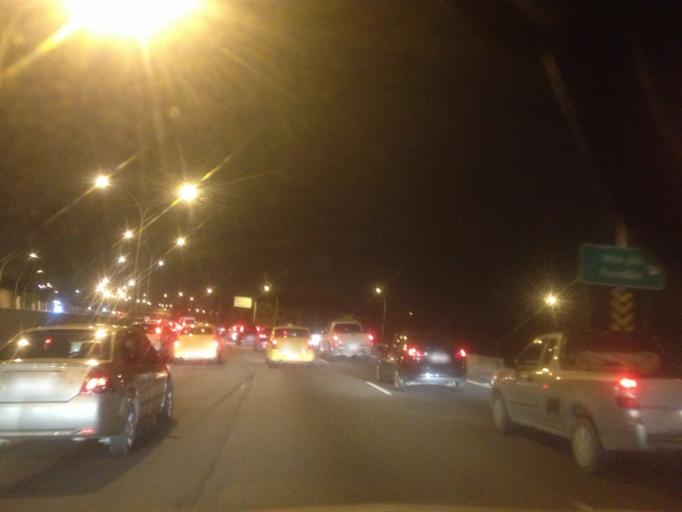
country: BR
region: Rio de Janeiro
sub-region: Rio De Janeiro
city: Rio de Janeiro
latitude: -22.8644
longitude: -43.2339
